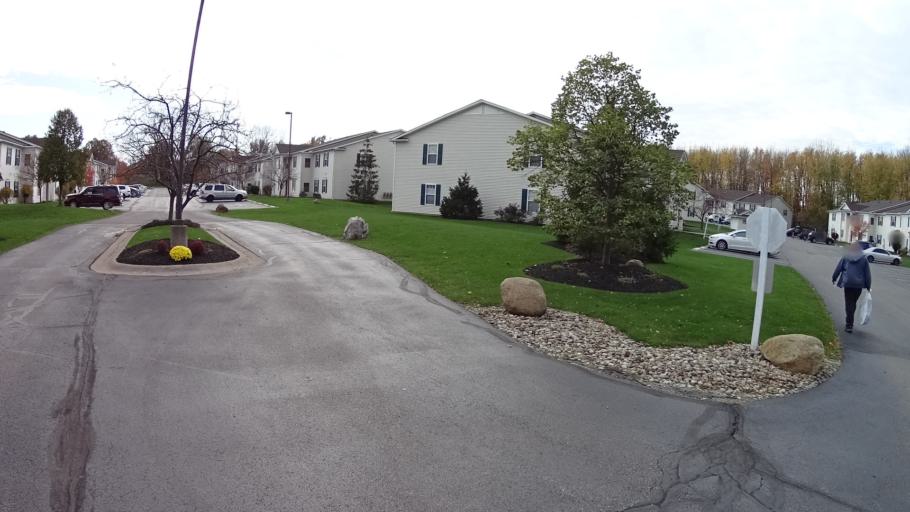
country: US
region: Ohio
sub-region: Lorain County
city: Sheffield Lake
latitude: 41.4805
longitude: -82.1291
